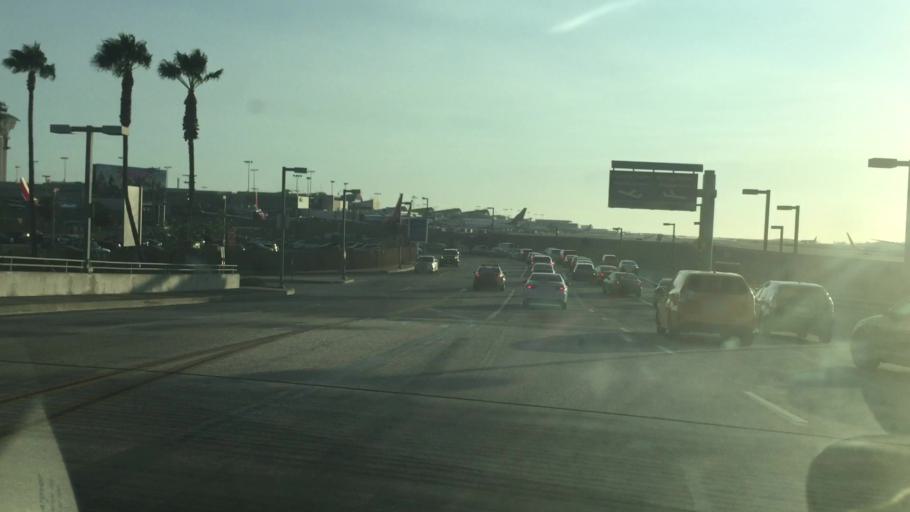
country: US
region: California
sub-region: Los Angeles County
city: El Segundo
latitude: 33.9488
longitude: -118.3976
